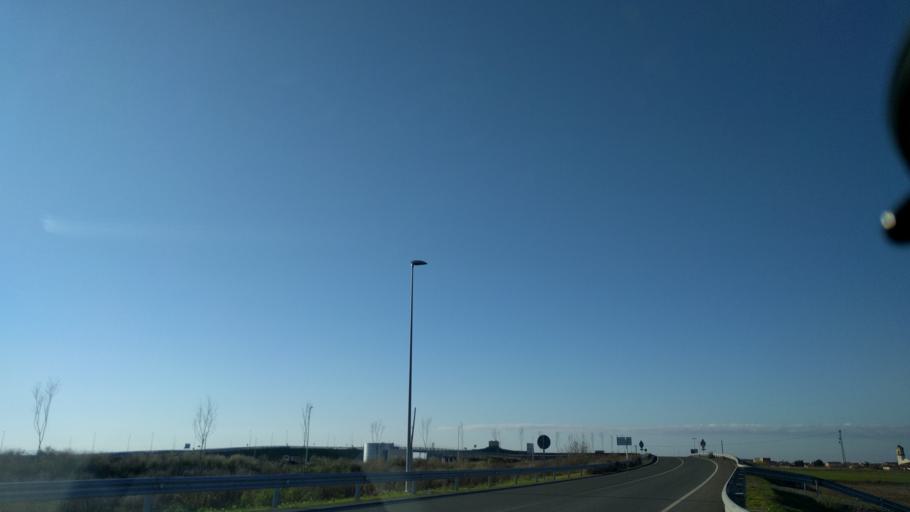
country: ES
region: Catalonia
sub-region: Provincia de Lleida
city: Termens
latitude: 41.6946
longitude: 0.7374
